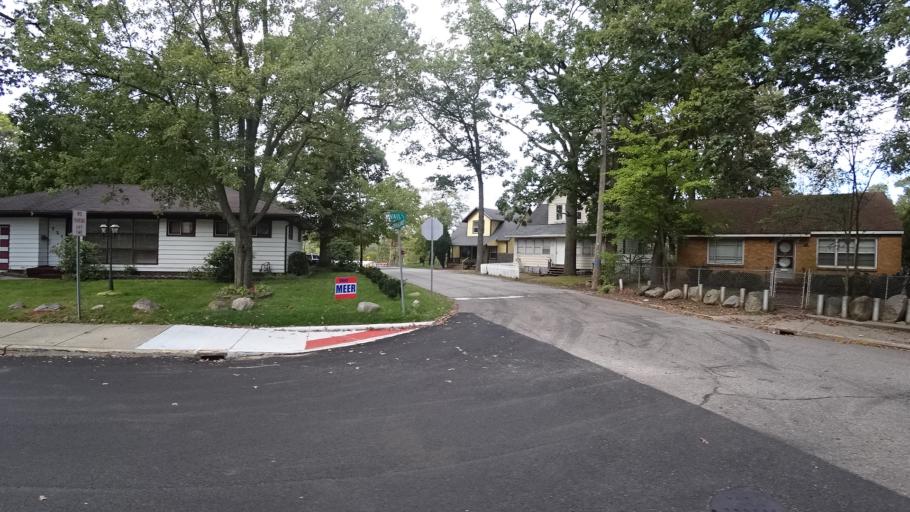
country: US
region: Indiana
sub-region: LaPorte County
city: Michigan City
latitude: 41.7169
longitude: -86.8825
